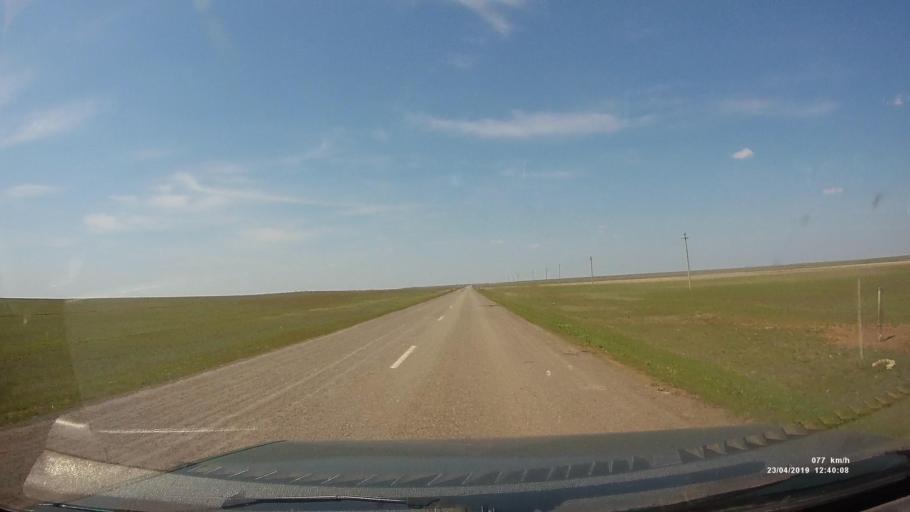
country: RU
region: Kalmykiya
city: Yashalta
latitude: 46.4385
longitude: 42.7001
